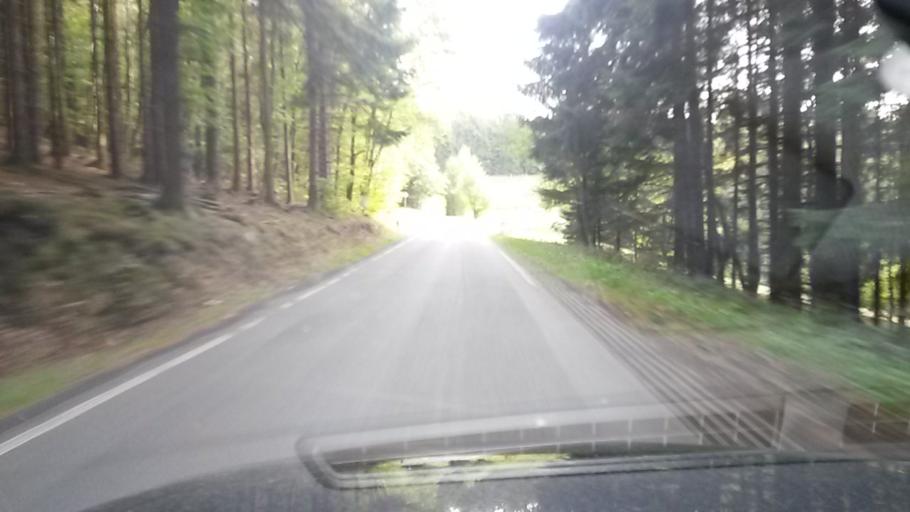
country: DE
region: North Rhine-Westphalia
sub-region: Regierungsbezirk Arnsberg
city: Herscheid
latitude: 51.2092
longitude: 7.7594
